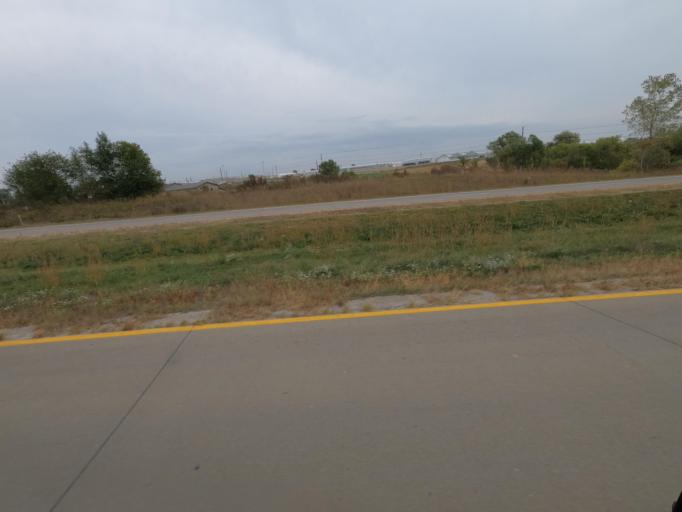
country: US
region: Iowa
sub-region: Marion County
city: Pella
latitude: 41.4048
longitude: -92.9412
